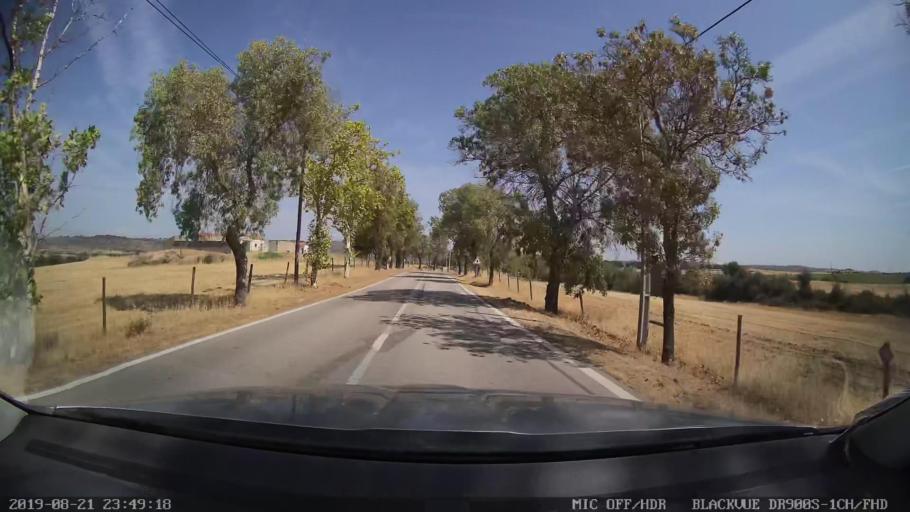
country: PT
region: Castelo Branco
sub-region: Idanha-A-Nova
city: Idanha-a-Nova
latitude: 39.8764
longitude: -7.2513
